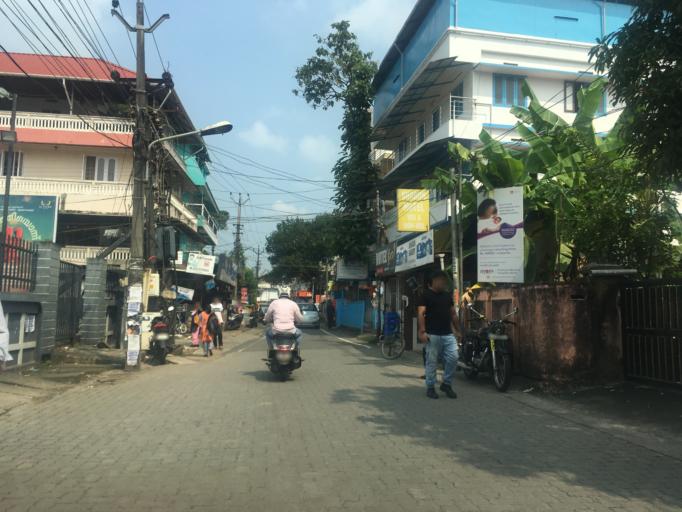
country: IN
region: Kerala
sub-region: Ernakulam
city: Elur
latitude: 10.0311
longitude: 76.3099
